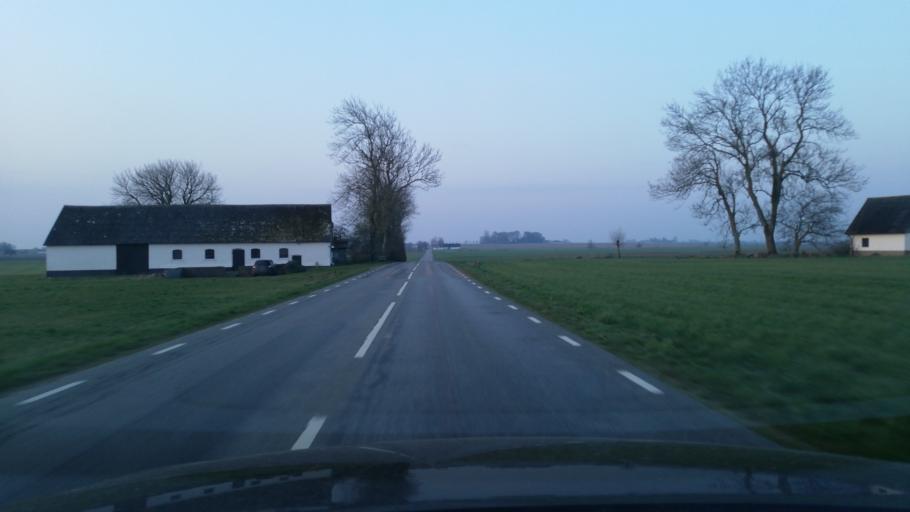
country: SE
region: Skane
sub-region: Tomelilla Kommun
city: Tomelilla
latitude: 55.4797
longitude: 14.1004
